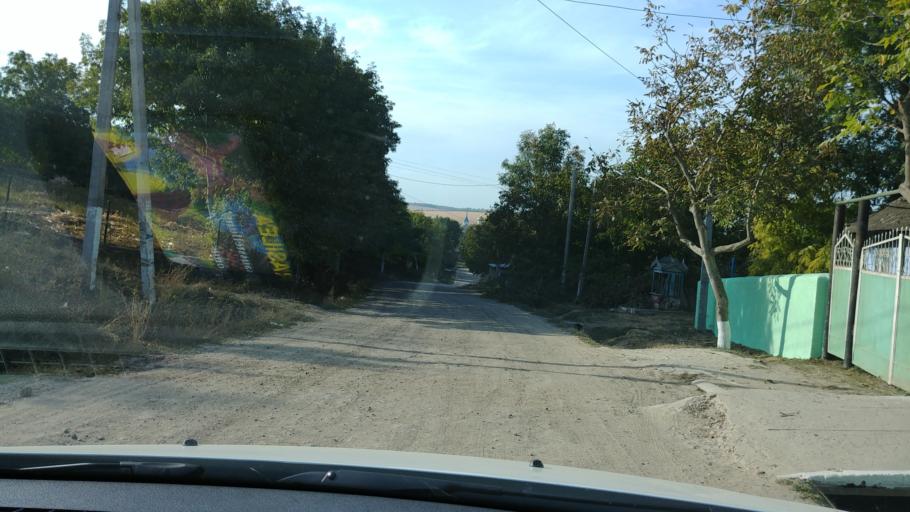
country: MD
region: Rezina
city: Rezina
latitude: 47.7461
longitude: 28.8876
